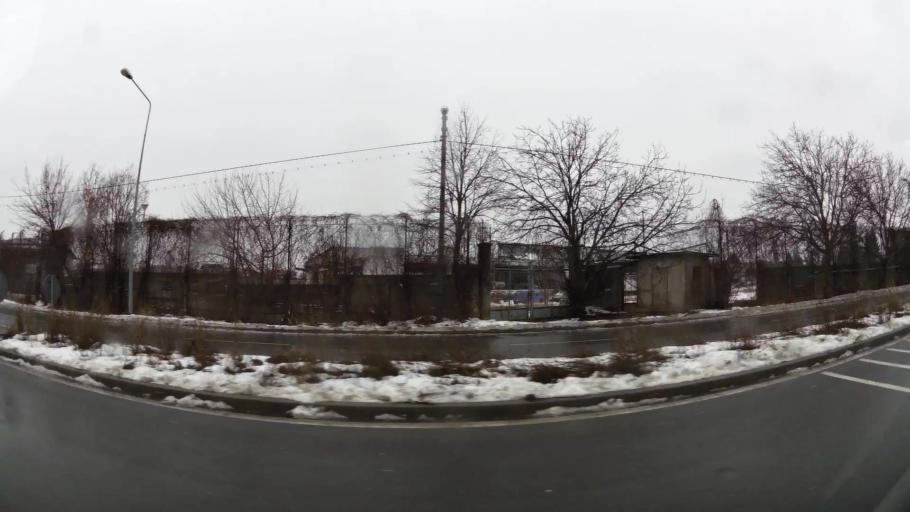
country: RO
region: Ilfov
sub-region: Comuna Chiajna
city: Rosu
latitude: 44.4893
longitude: 26.0577
